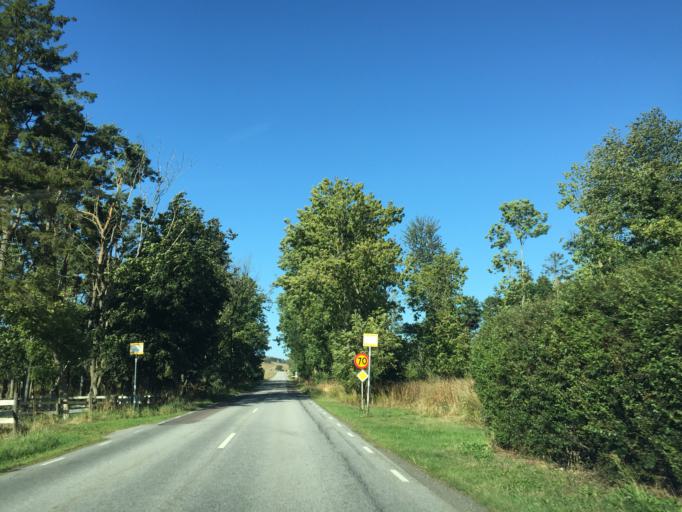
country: SE
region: Skane
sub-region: Ystads Kommun
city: Kopingebro
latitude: 55.3906
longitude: 14.0998
